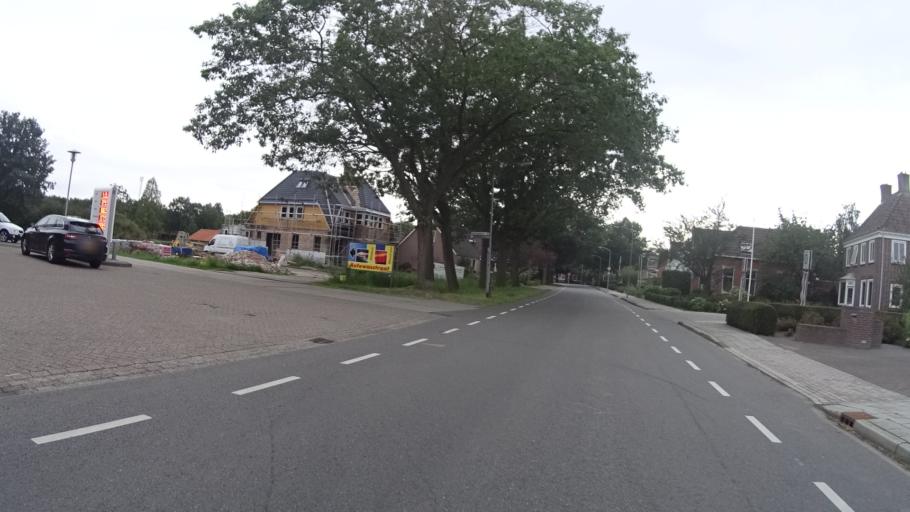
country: NL
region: Groningen
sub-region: Gemeente Slochteren
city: Slochteren
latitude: 53.2218
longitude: 6.8063
